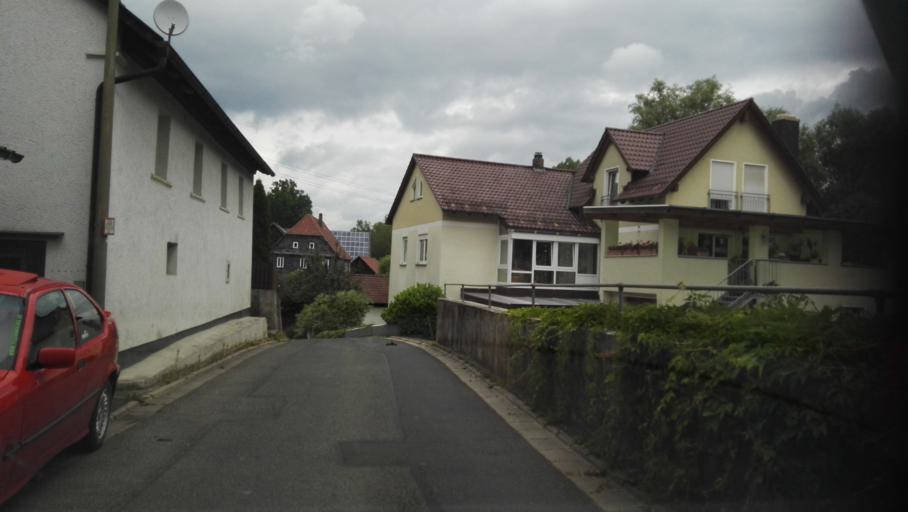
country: DE
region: Bavaria
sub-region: Upper Franconia
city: Marktgraitz
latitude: 50.1820
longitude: 11.1983
